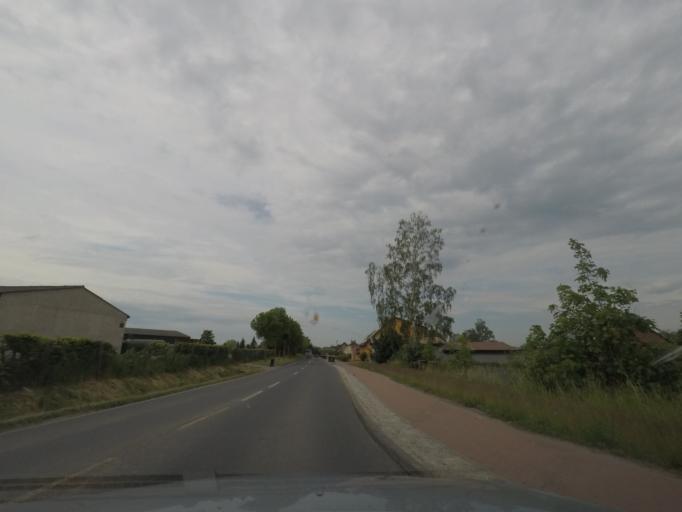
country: DE
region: Brandenburg
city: Schenkenberg
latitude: 53.3489
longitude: 13.9561
